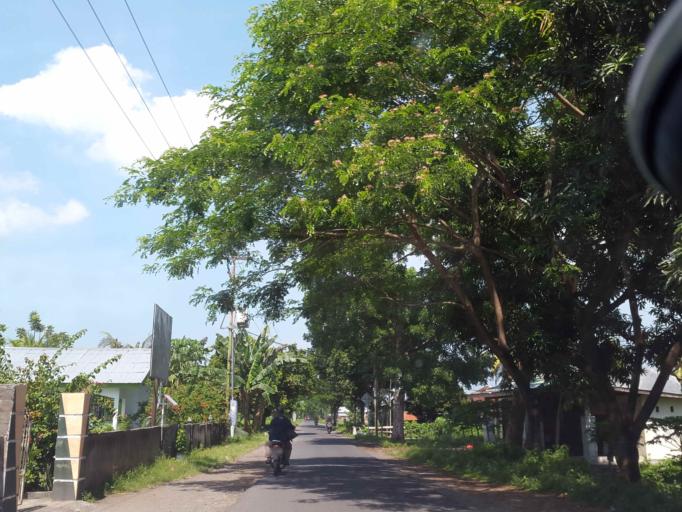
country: ID
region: West Nusa Tenggara
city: Mambalan
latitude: -8.5496
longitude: 116.1266
